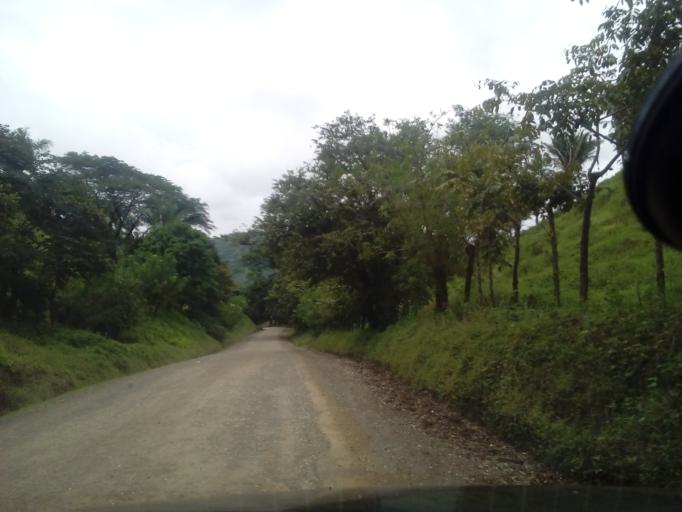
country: CR
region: Guanacaste
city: Samara
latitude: 9.9187
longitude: -85.5719
